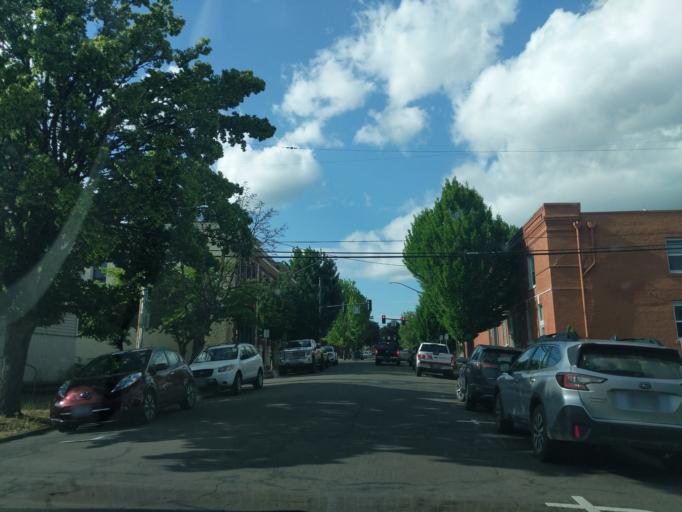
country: US
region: Oregon
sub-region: Yamhill County
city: Newberg
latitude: 45.2996
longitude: -122.9751
